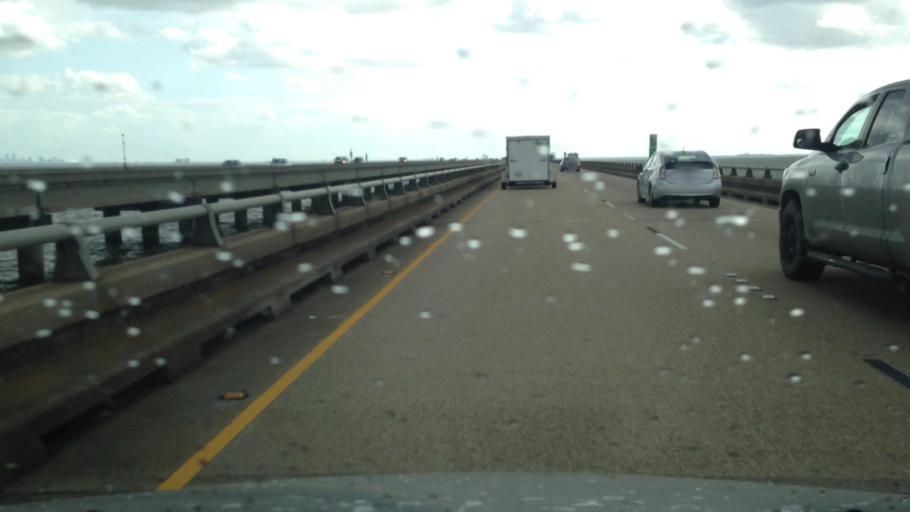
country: US
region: Louisiana
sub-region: Jefferson Parish
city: Metairie
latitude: 30.1128
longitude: -90.1382
